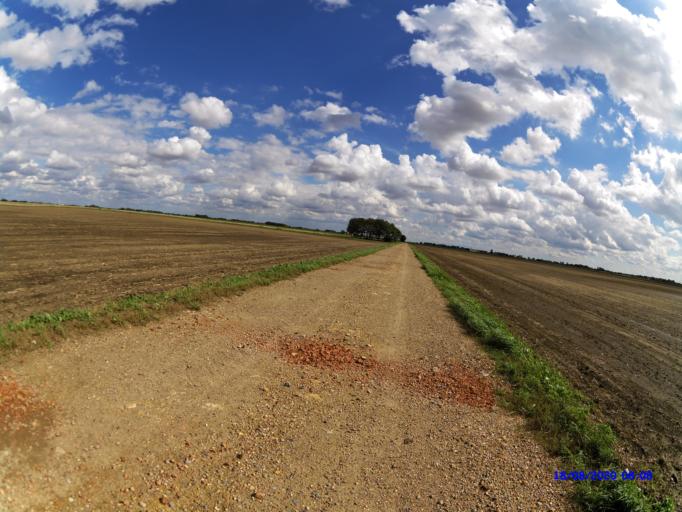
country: GB
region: England
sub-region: Cambridgeshire
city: Whittlesey
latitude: 52.5127
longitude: -0.0838
